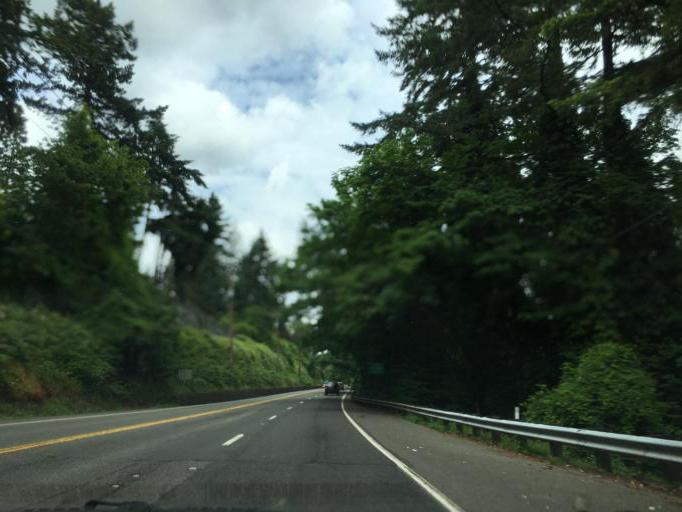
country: US
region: Oregon
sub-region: Clackamas County
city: Lake Oswego
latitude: 45.4321
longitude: -122.6552
